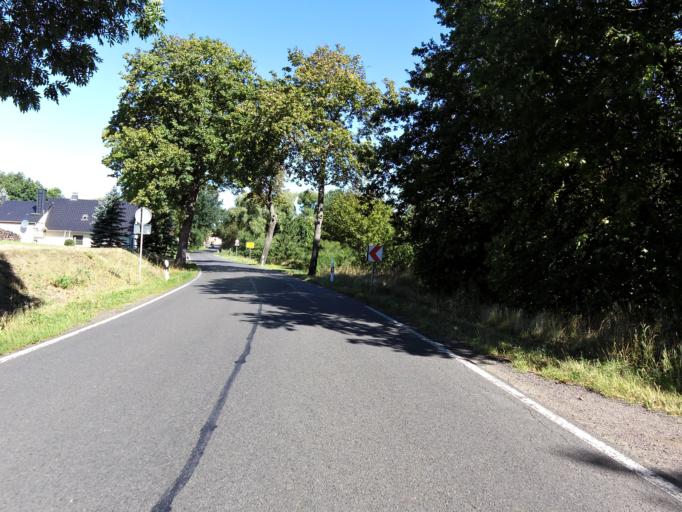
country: DE
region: Saxony-Anhalt
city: Pretzsch
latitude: 51.6839
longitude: 12.8272
